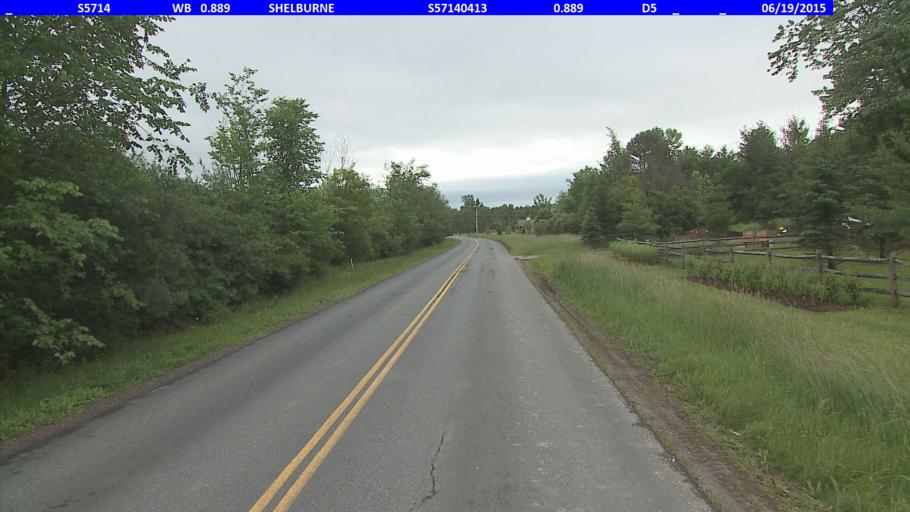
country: US
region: Vermont
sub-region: Chittenden County
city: Burlington
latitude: 44.3850
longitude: -73.2435
